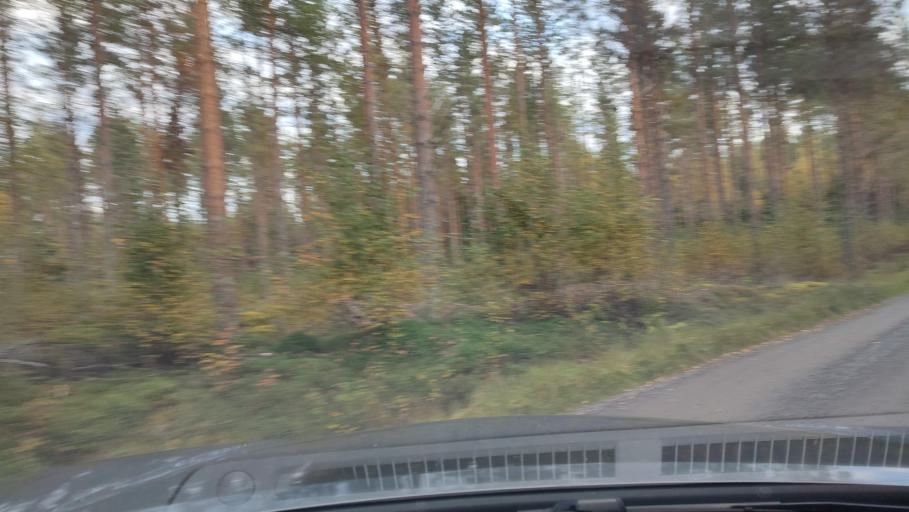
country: FI
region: Ostrobothnia
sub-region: Sydosterbotten
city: Kristinestad
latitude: 62.2364
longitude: 21.3993
